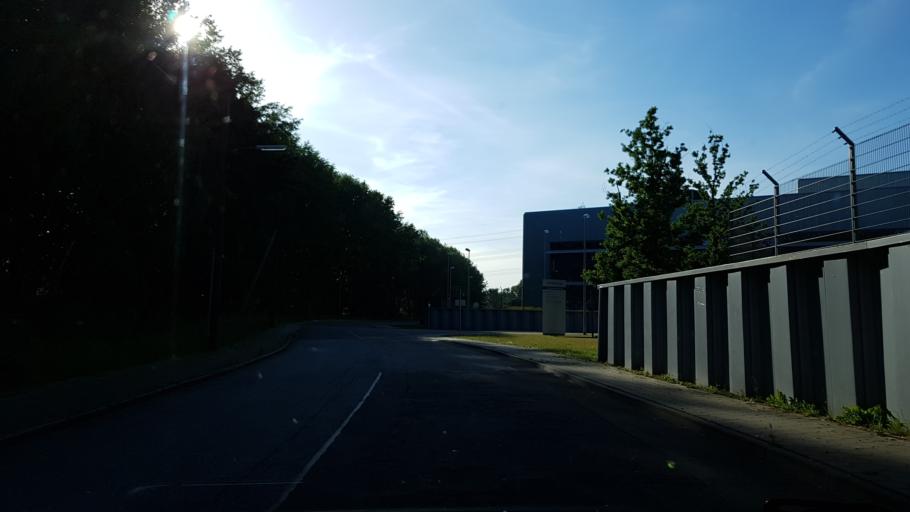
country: DE
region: Hamburg
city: Harburg
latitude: 53.4871
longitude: 9.9489
